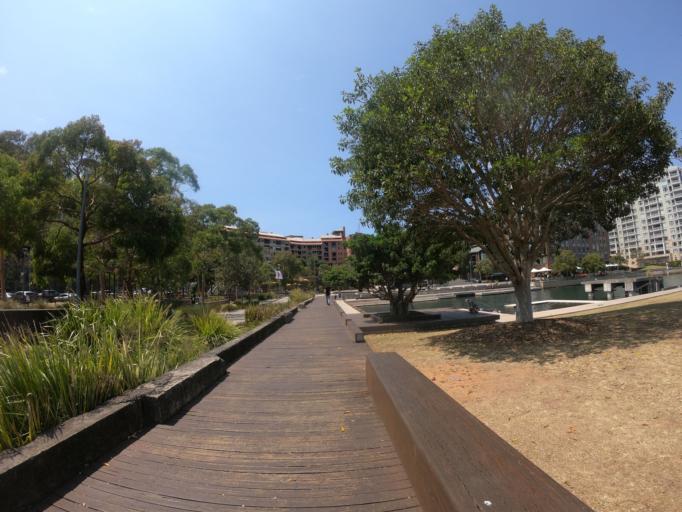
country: AU
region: New South Wales
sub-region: Leichhardt
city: Balmain East
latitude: -33.8648
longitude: 151.1917
